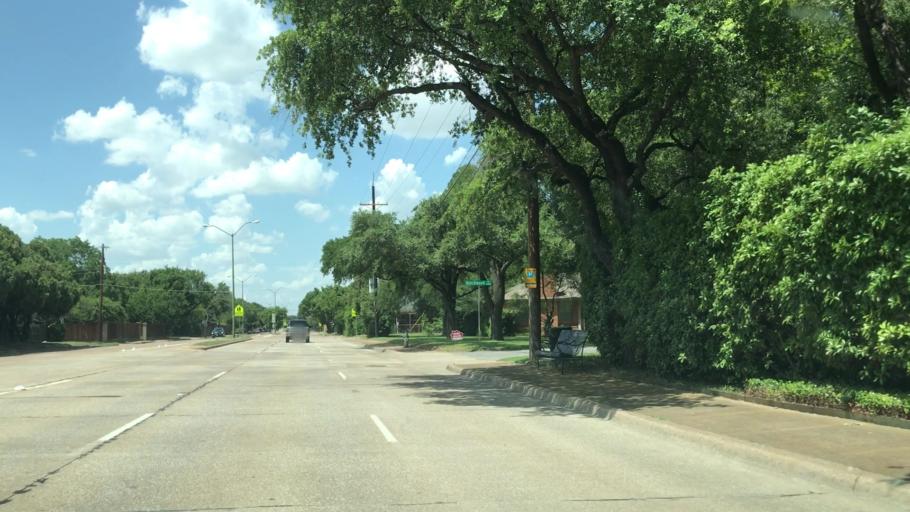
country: US
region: Texas
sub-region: Dallas County
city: University Park
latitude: 32.8752
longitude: -96.8384
